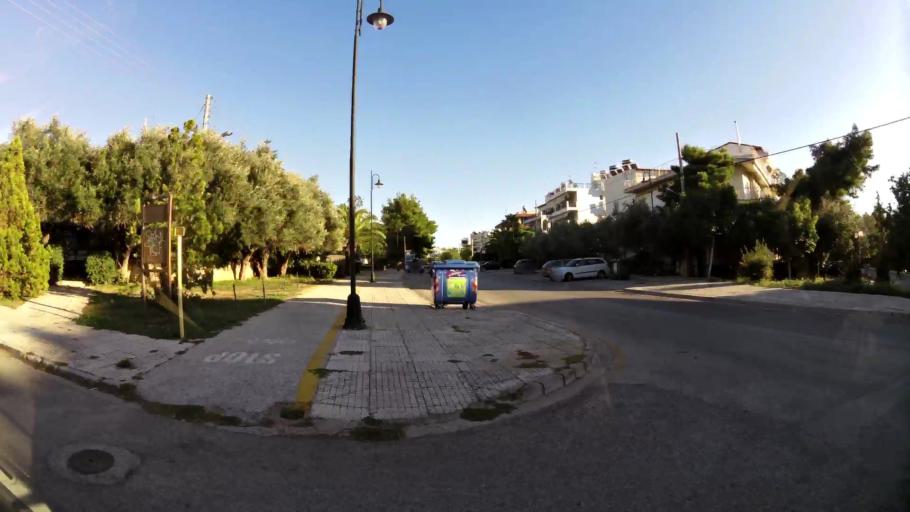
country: GR
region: Attica
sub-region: Nomarchia Athinas
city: Glyfada
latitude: 37.8648
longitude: 23.7597
